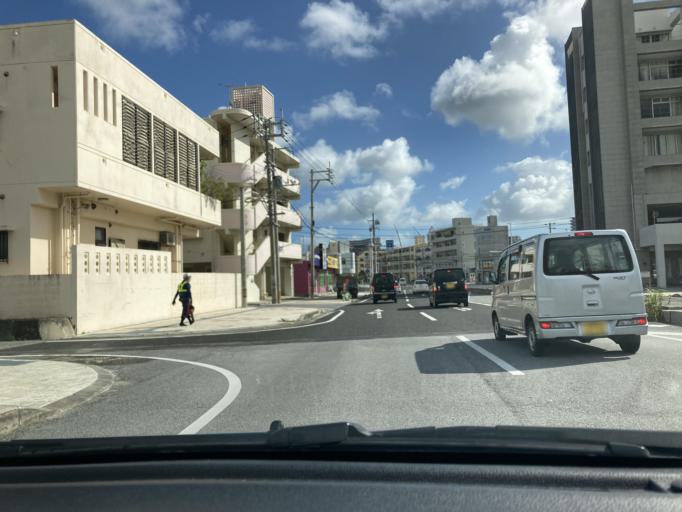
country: JP
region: Okinawa
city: Tomigusuku
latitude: 26.1966
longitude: 127.7270
